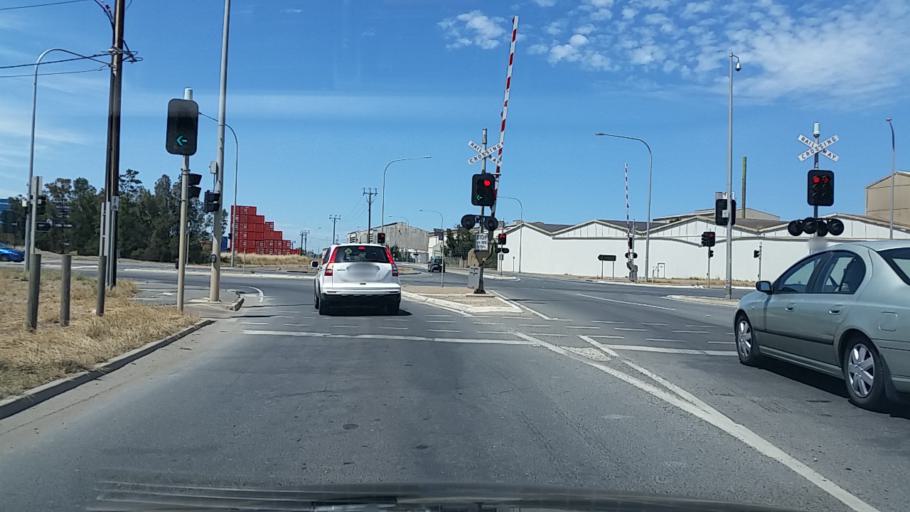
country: AU
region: South Australia
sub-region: Port Adelaide Enfield
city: Birkenhead
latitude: -34.8356
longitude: 138.5150
